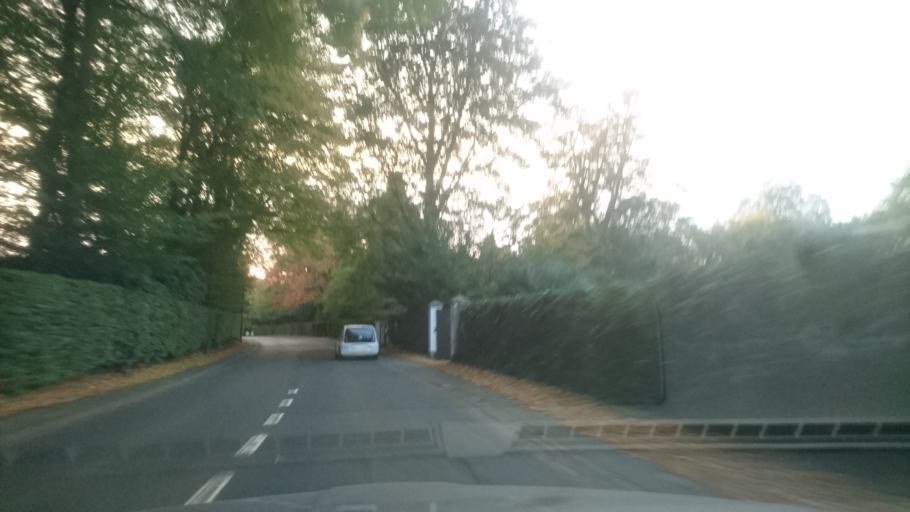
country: BE
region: Flanders
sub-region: Provincie Vlaams-Brabant
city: Sint-Genesius-Rode
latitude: 50.7649
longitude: 4.3770
